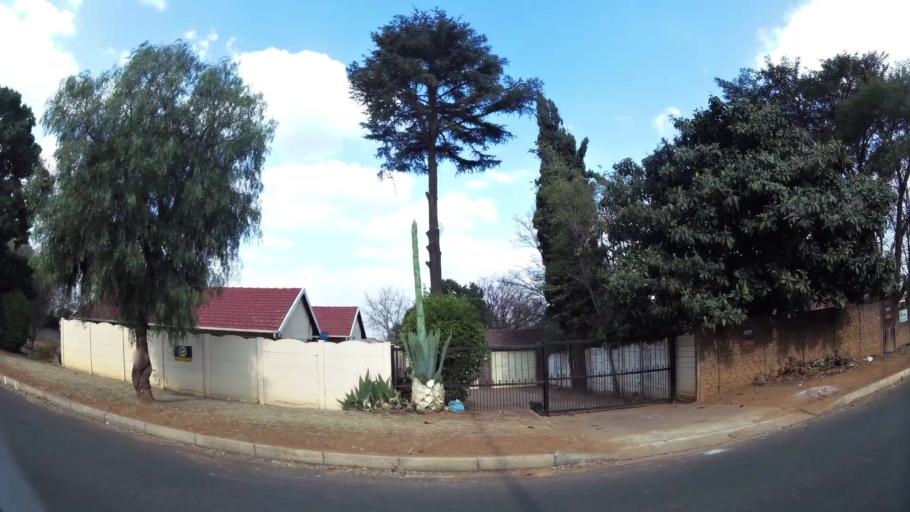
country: ZA
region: Gauteng
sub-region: Ekurhuleni Metropolitan Municipality
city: Germiston
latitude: -26.2475
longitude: 28.1817
